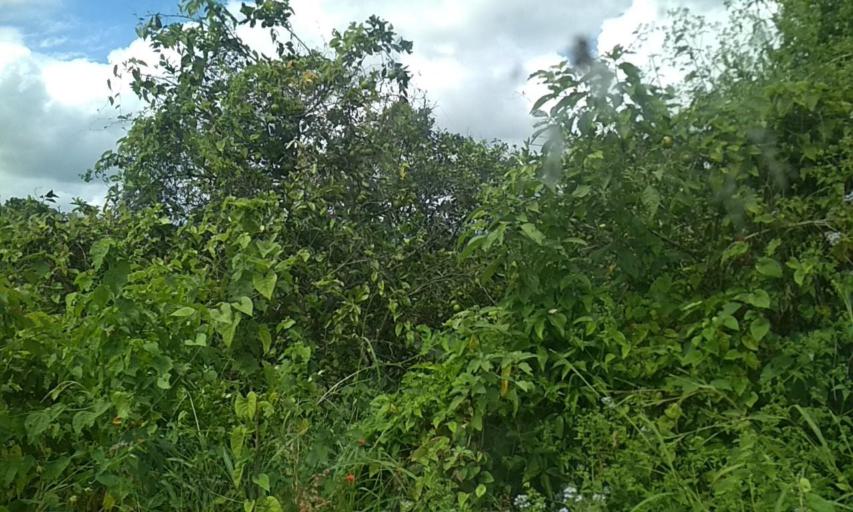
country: MX
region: Puebla
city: San Jose Acateno
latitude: 20.2707
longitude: -97.1291
